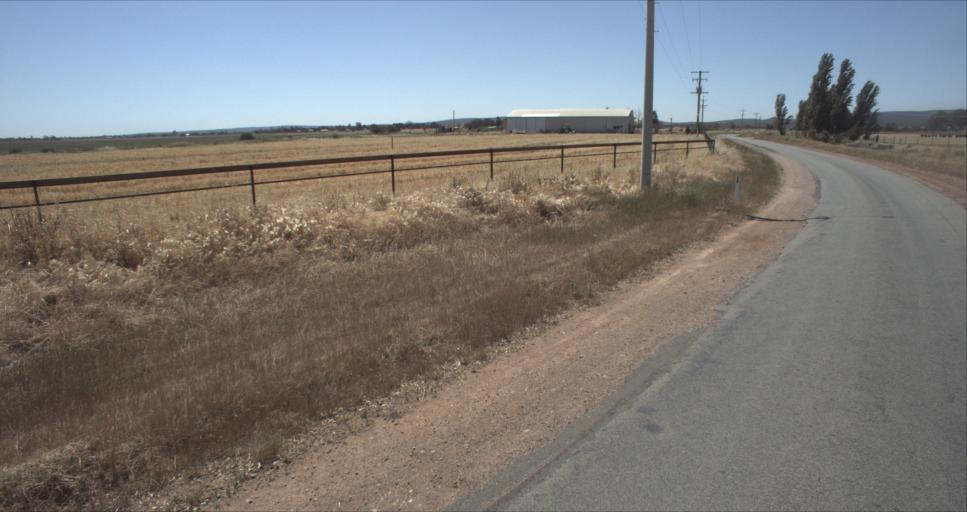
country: AU
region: New South Wales
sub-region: Leeton
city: Leeton
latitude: -34.5394
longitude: 146.4414
